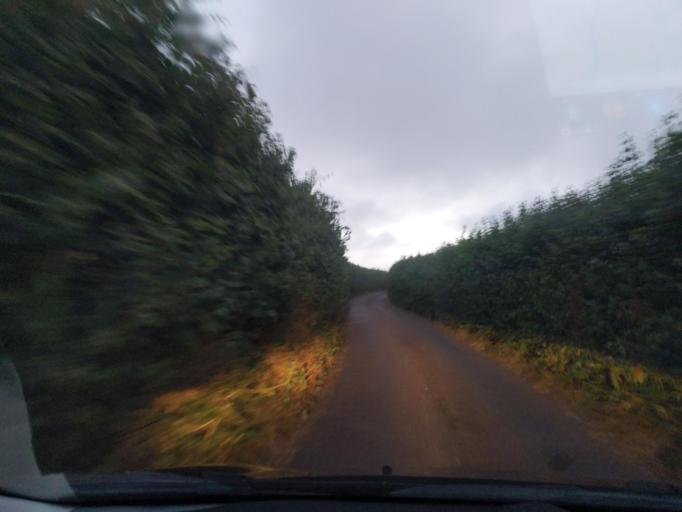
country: GB
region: England
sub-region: Devon
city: Marldon
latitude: 50.4656
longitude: -3.6086
